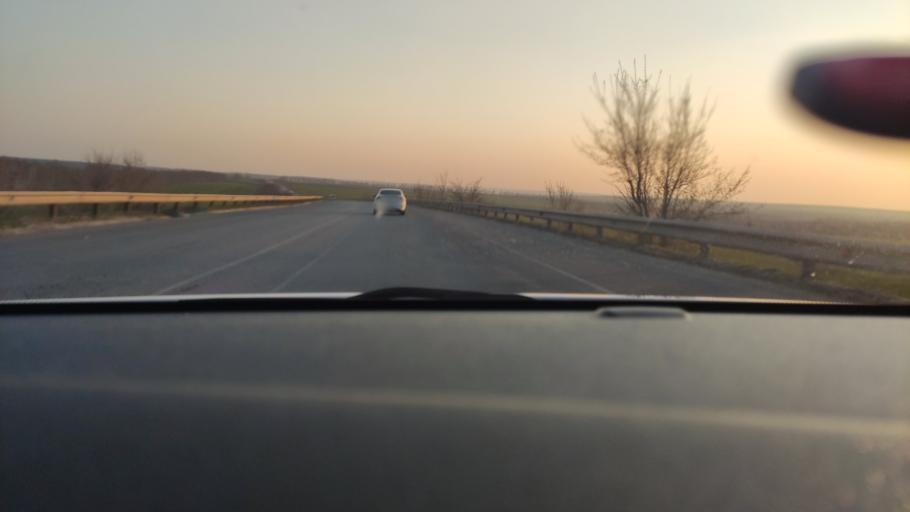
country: RU
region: Voronezj
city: Kolodeznyy
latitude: 51.4079
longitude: 39.2455
